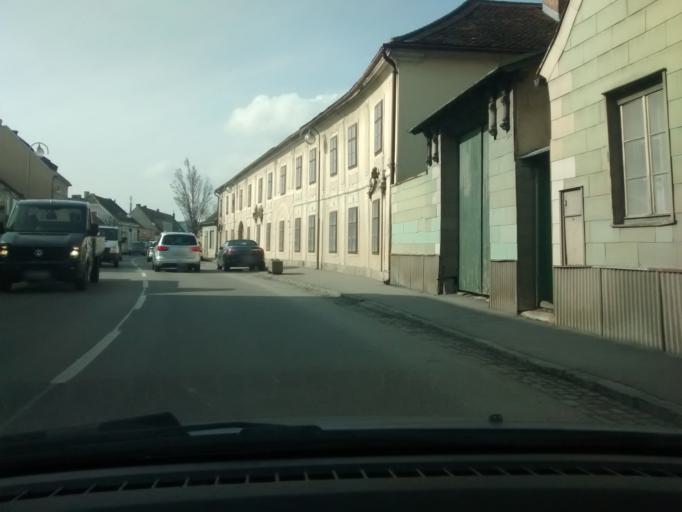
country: AT
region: Lower Austria
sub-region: Politischer Bezirk Baden
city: Traiskirchen
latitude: 48.0167
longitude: 16.2936
